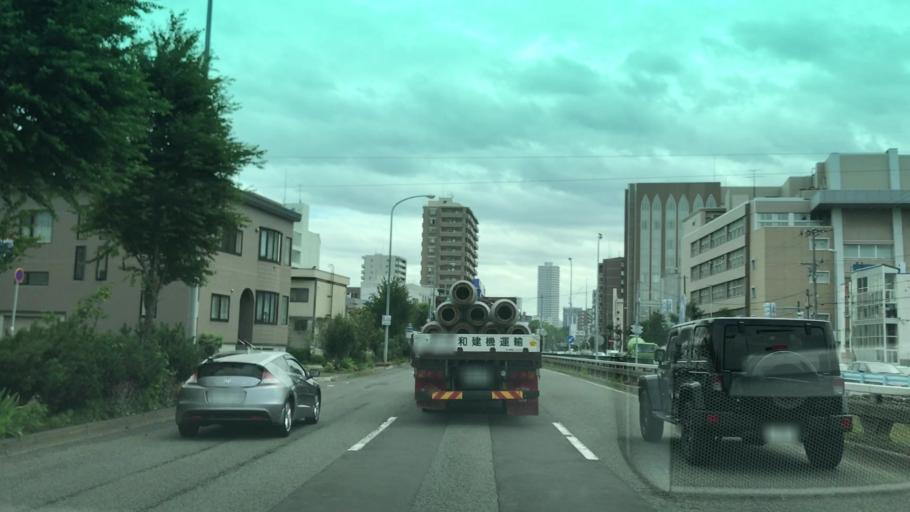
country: JP
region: Hokkaido
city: Sapporo
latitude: 43.0818
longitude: 141.3507
